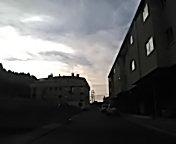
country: ES
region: Castille and Leon
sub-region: Provincia de Soria
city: San Leonardo de Yague
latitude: 41.8323
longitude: -3.0736
